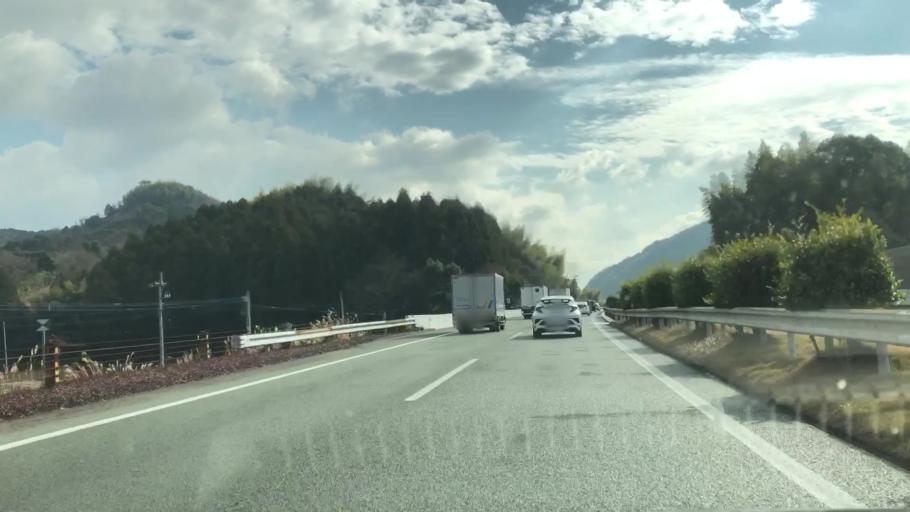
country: JP
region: Fukuoka
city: Setakamachi-takayanagi
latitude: 33.1065
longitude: 130.5340
